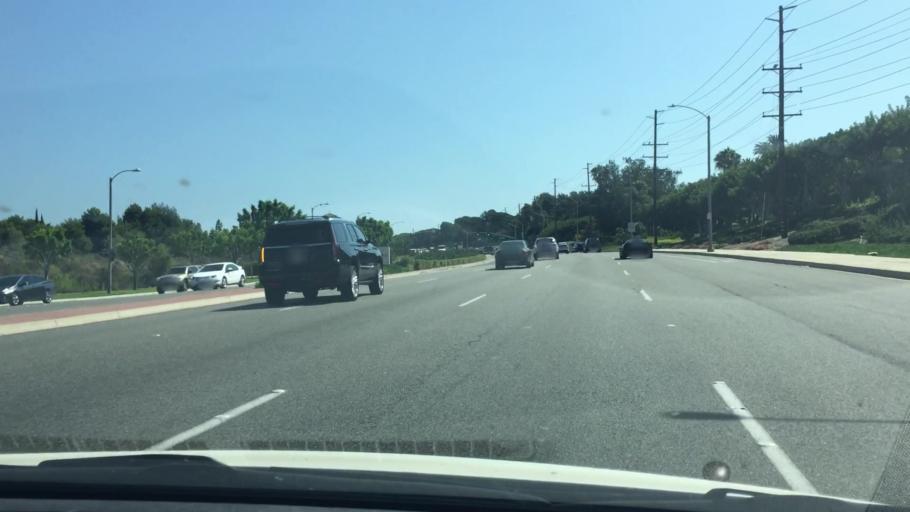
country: US
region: California
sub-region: Orange County
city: San Joaquin Hills
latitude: 33.6365
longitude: -117.8625
